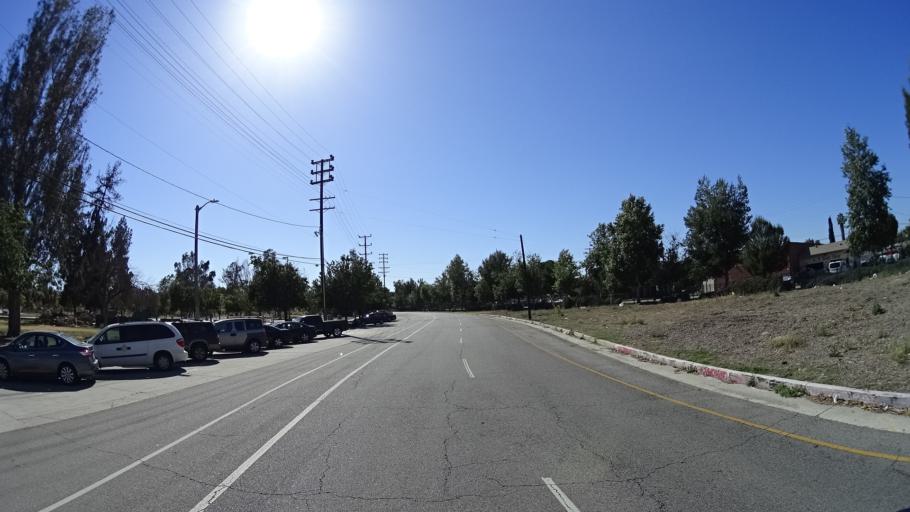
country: US
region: California
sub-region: Los Angeles County
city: North Hollywood
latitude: 34.1682
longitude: -118.3816
